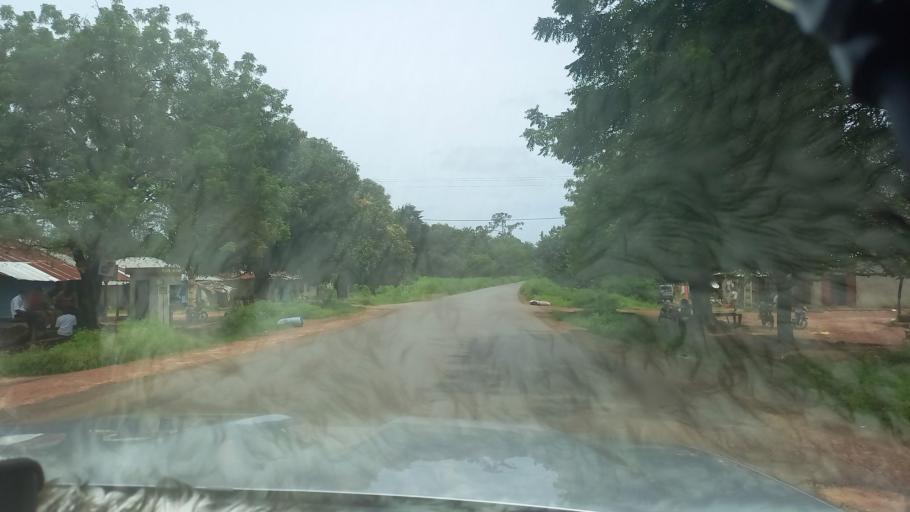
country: SN
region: Kolda
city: Marsassoum
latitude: 12.9545
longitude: -16.0061
